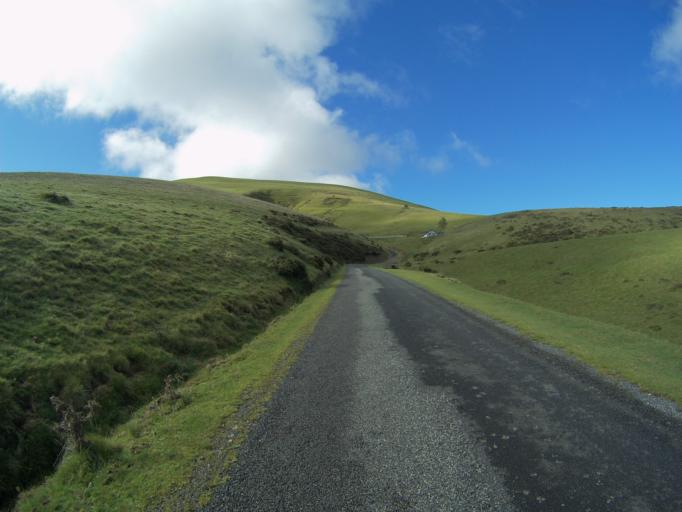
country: FR
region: Aquitaine
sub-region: Departement des Pyrenees-Atlantiques
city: Saint-Jean-Pied-de-Port
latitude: 43.0942
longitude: -1.2429
